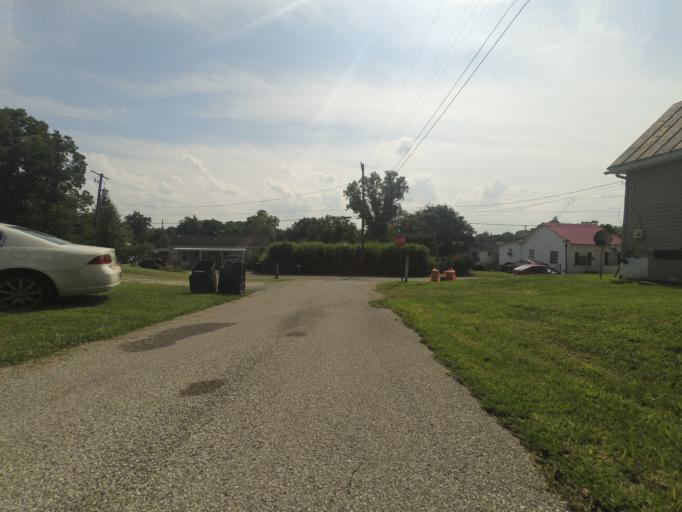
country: US
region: West Virginia
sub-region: Cabell County
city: Huntington
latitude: 38.4173
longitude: -82.4013
